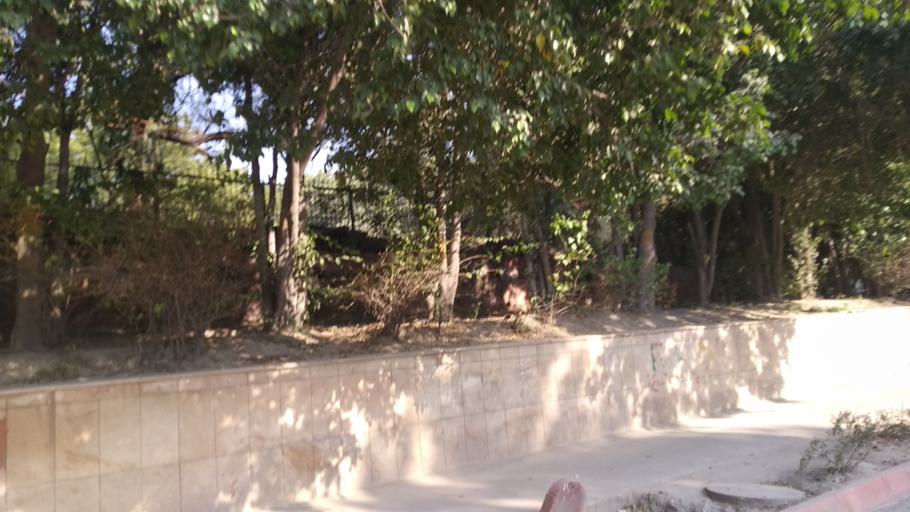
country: IN
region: NCT
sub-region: New Delhi
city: New Delhi
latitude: 28.6134
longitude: 77.2404
